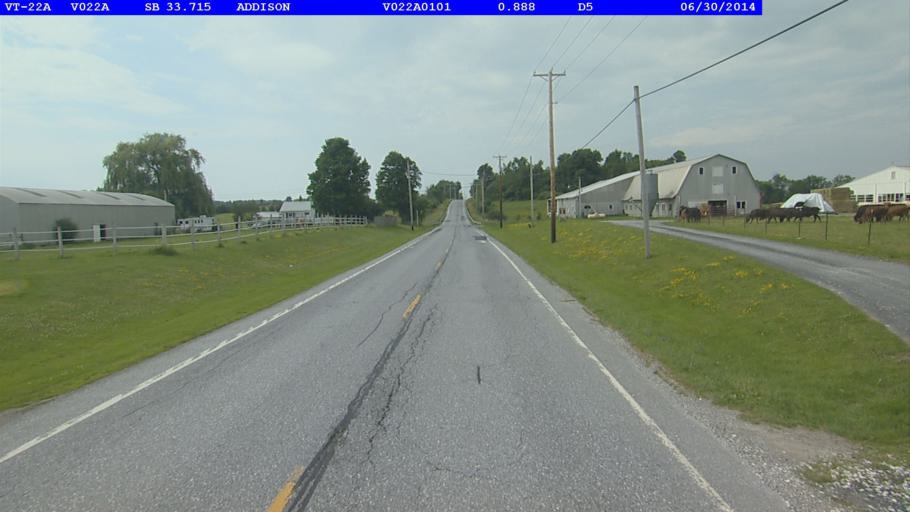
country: US
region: Vermont
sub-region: Addison County
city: Vergennes
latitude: 44.0426
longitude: -73.3049
